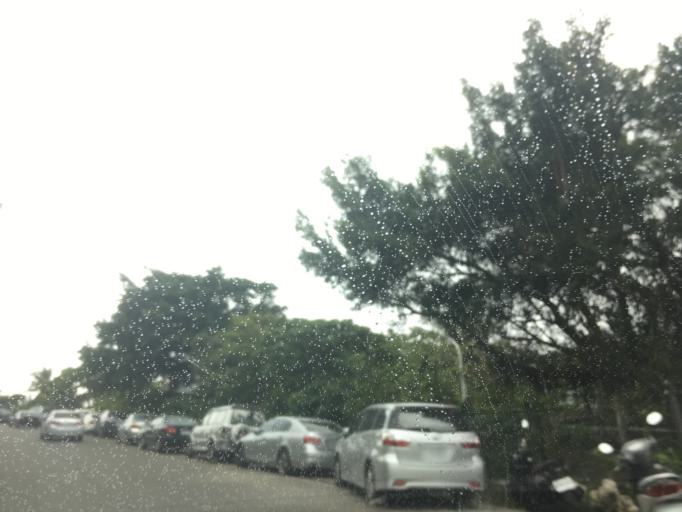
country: TW
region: Taiwan
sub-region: Taitung
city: Taitung
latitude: 22.7931
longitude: 121.1953
